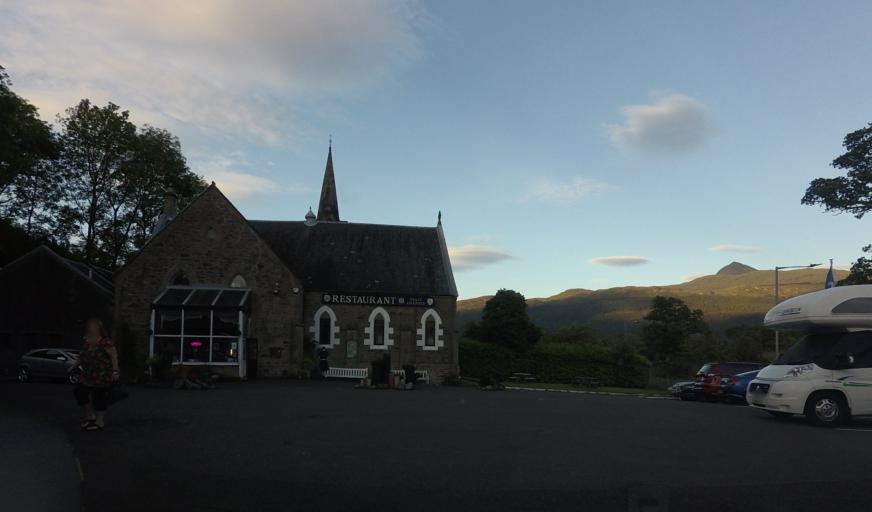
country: GB
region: Scotland
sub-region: Argyll and Bute
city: Garelochhead
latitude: 56.2029
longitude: -4.7206
